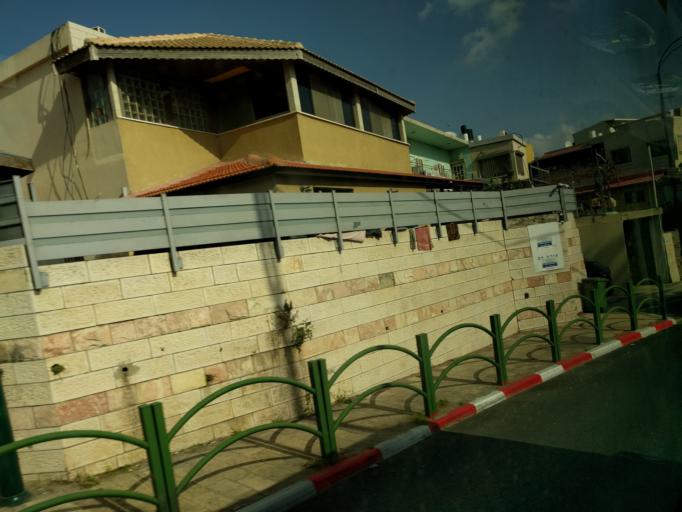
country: IL
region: Haifa
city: Daliyat el Karmil
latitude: 32.7191
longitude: 35.0643
